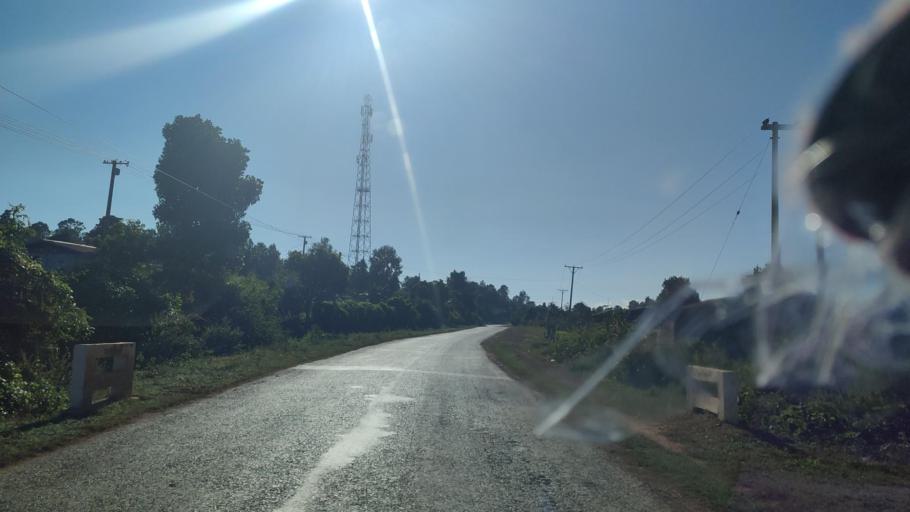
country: MM
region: Shan
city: Taunggyi
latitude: 20.9358
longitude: 97.6237
